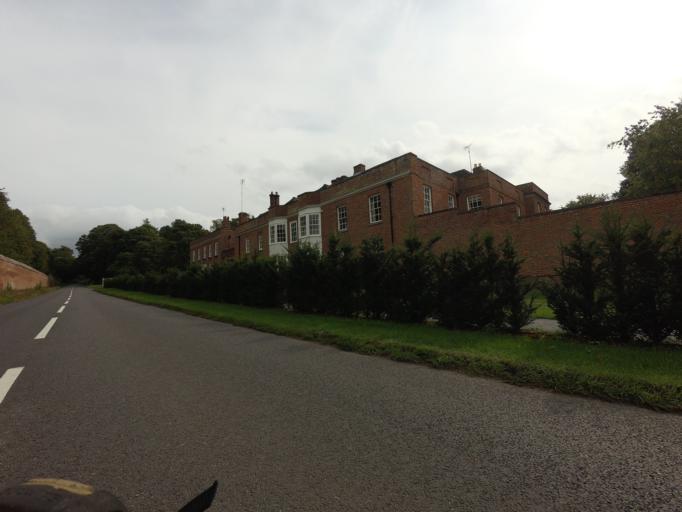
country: GB
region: England
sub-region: Essex
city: Saffron Walden
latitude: 52.0196
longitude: 0.2194
